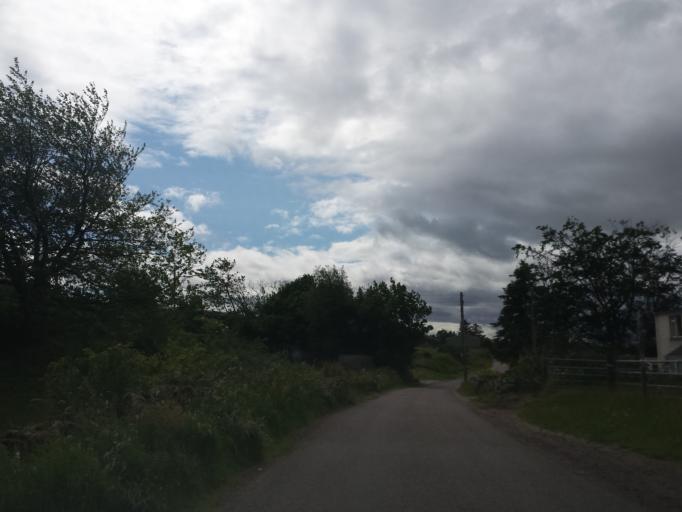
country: GB
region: Scotland
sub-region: Highland
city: Nairn
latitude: 57.5091
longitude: -3.9825
